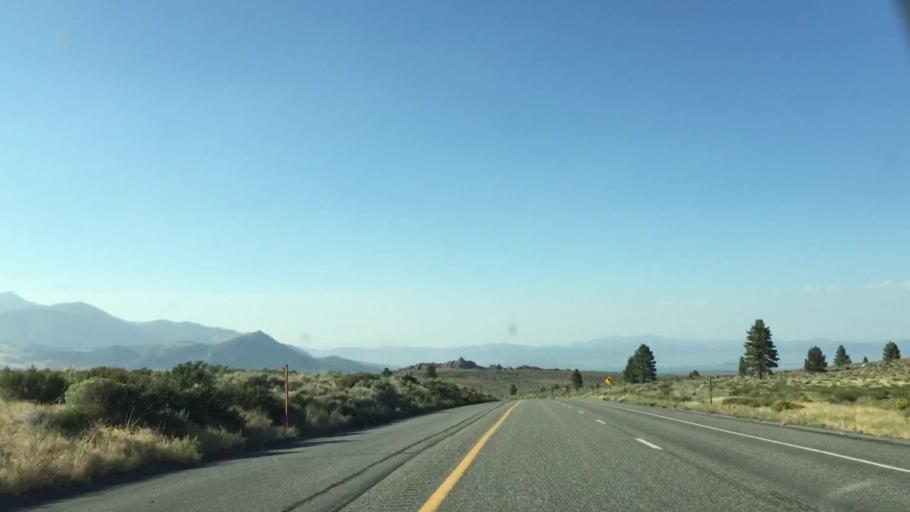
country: US
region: California
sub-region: Mono County
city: Mammoth Lakes
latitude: 37.8357
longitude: -119.0697
